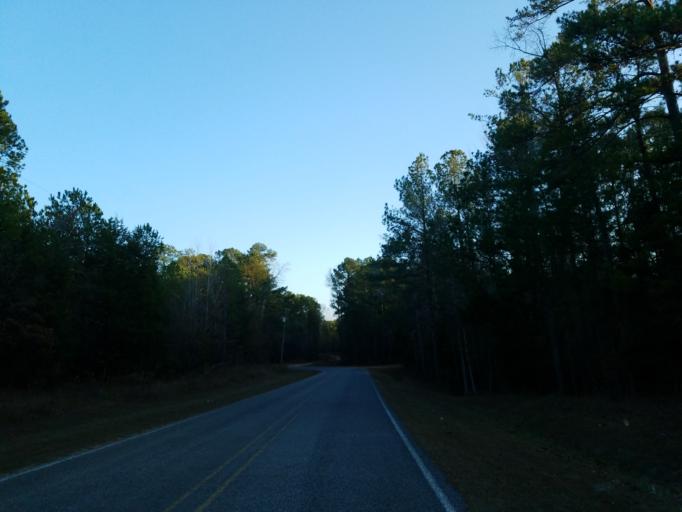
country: US
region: Mississippi
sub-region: Clarke County
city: Stonewall
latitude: 32.2632
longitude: -88.8096
